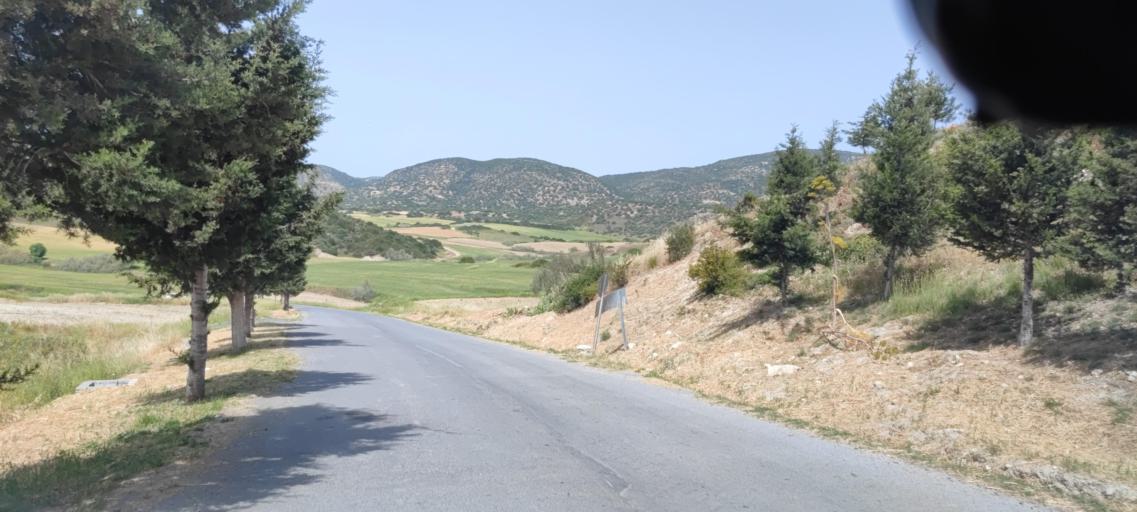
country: CY
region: Ammochostos
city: Rizokarpaso
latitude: 35.5118
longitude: 34.2706
